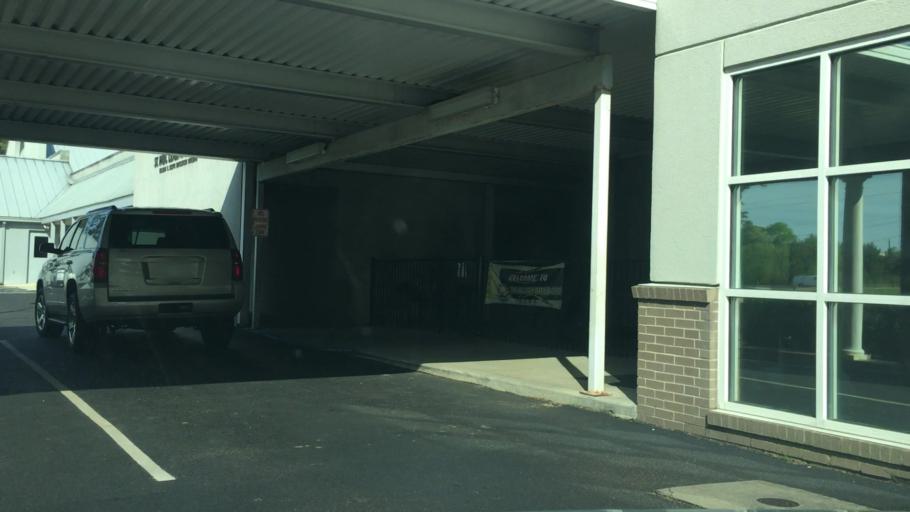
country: US
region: Mississippi
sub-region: Rankin County
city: Brandon
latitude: 32.3653
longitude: -89.9864
